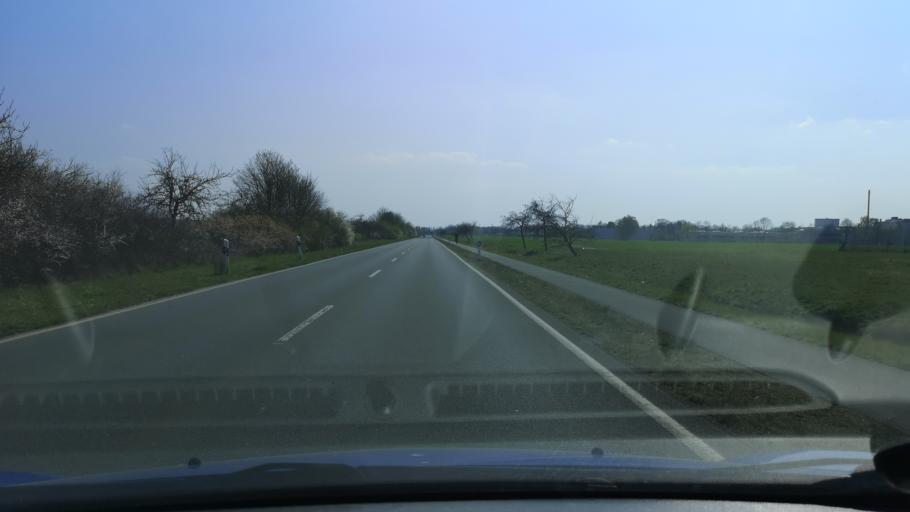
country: DE
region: Lower Saxony
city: Neustadt am Rubenberge
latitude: 52.5177
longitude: 9.4762
